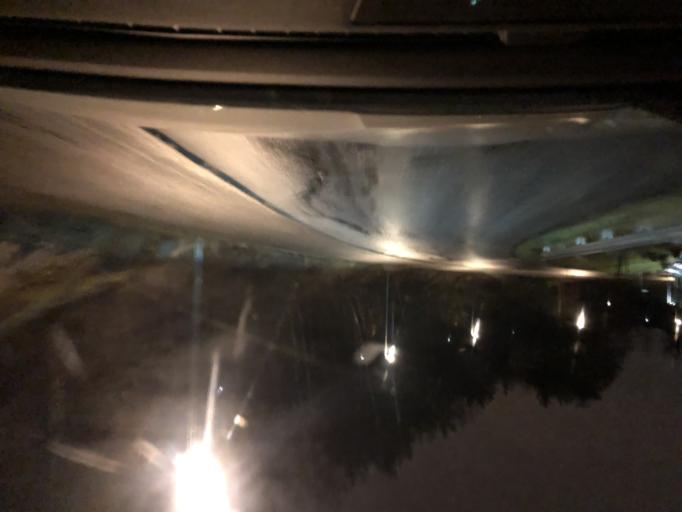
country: SE
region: Stockholm
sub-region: Jarfalla Kommun
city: Jakobsberg
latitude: 59.4025
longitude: 17.8078
